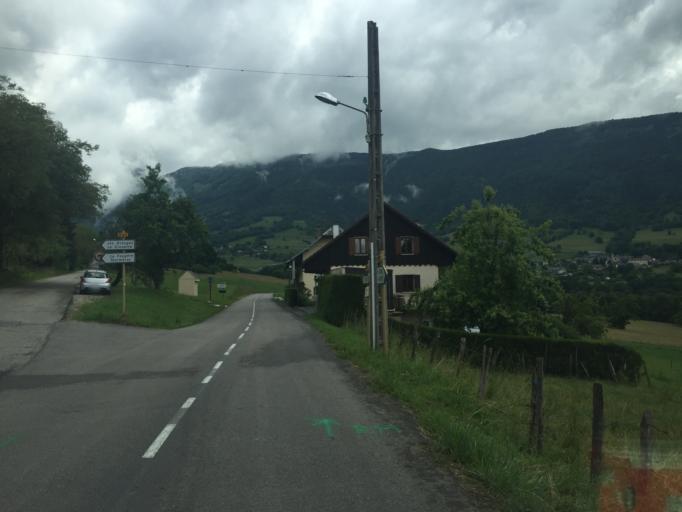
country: FR
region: Rhone-Alpes
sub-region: Departement de la Savoie
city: Barby
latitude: 45.5880
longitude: 6.0116
